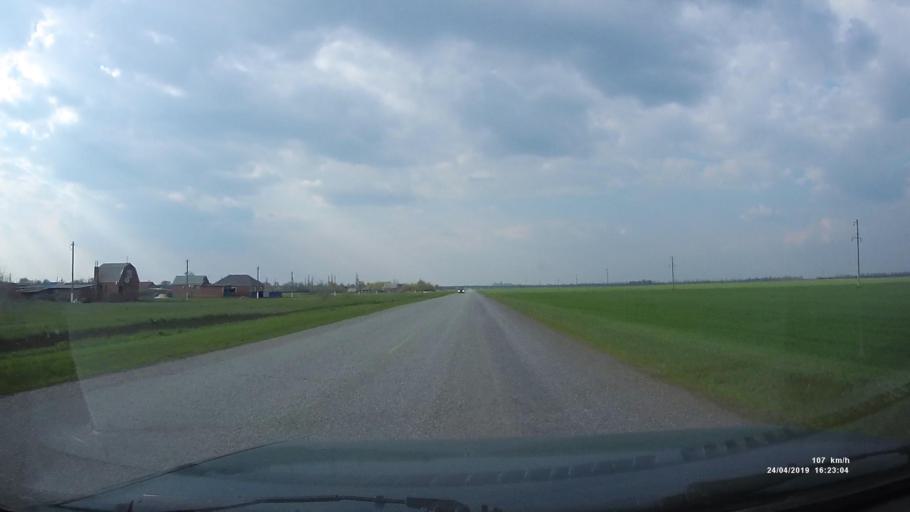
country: RU
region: Rostov
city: Orlovskiy
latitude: 46.8290
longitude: 42.0516
